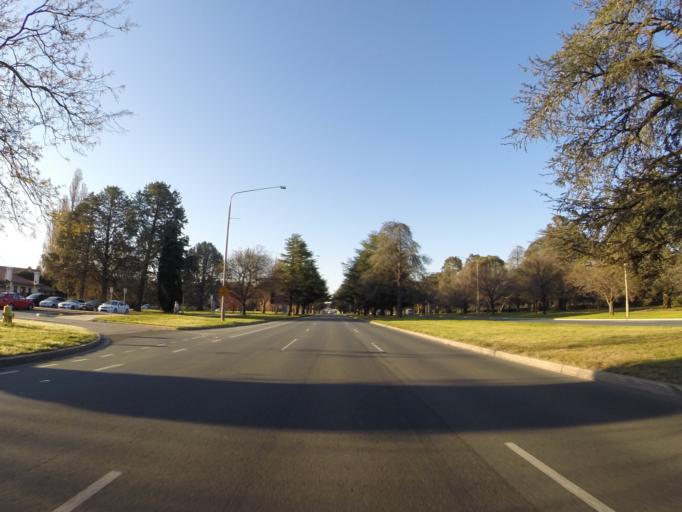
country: AU
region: Australian Capital Territory
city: Forrest
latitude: -35.3000
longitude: 149.1256
